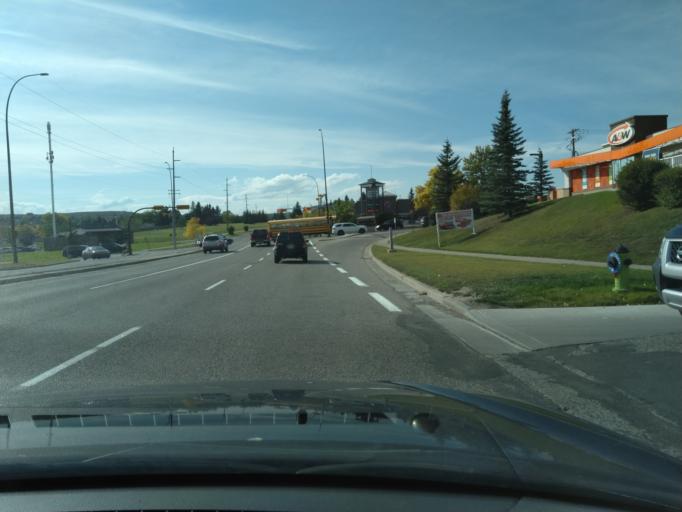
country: CA
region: Alberta
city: Calgary
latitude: 51.1253
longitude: -114.0705
